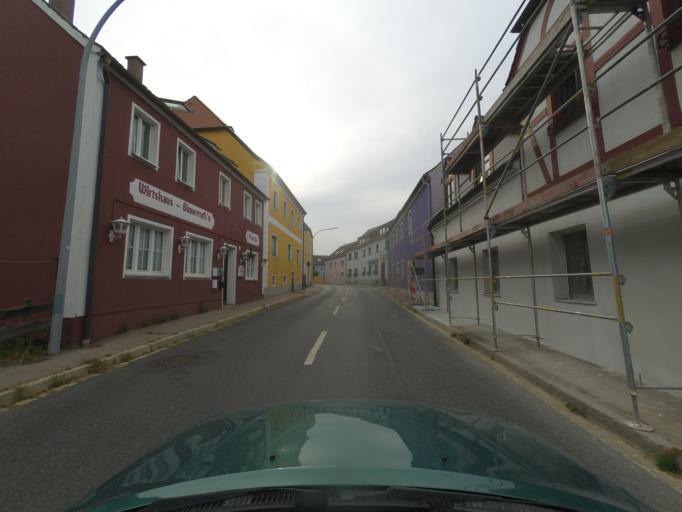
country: DE
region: Bavaria
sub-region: Upper Palatinate
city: Moosbach
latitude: 49.5915
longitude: 12.4076
